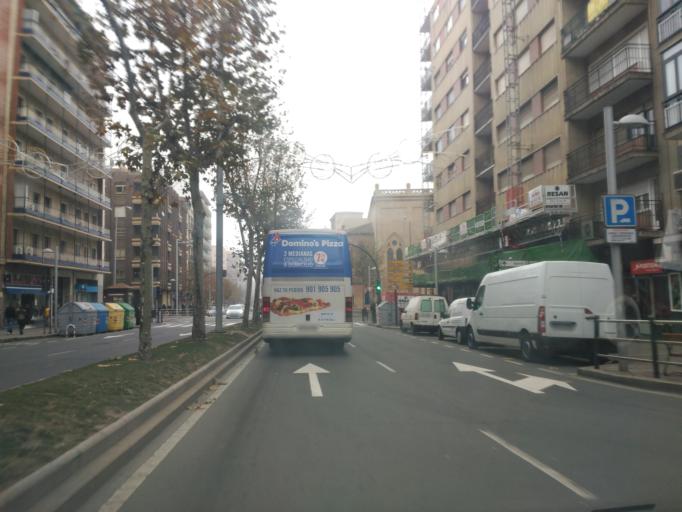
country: ES
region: Castille and Leon
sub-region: Provincia de Salamanca
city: Salamanca
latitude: 40.9714
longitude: -5.6589
